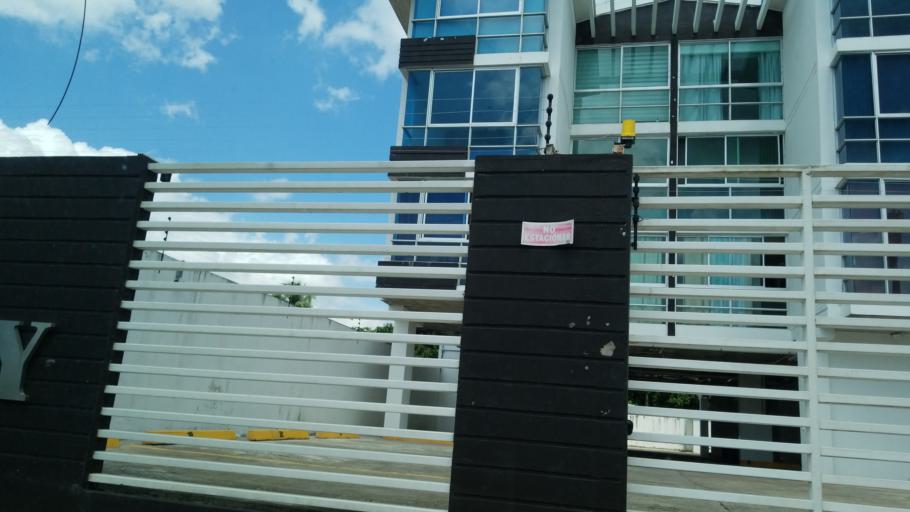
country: PA
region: Panama
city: San Miguelito
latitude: 9.0449
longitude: -79.4322
